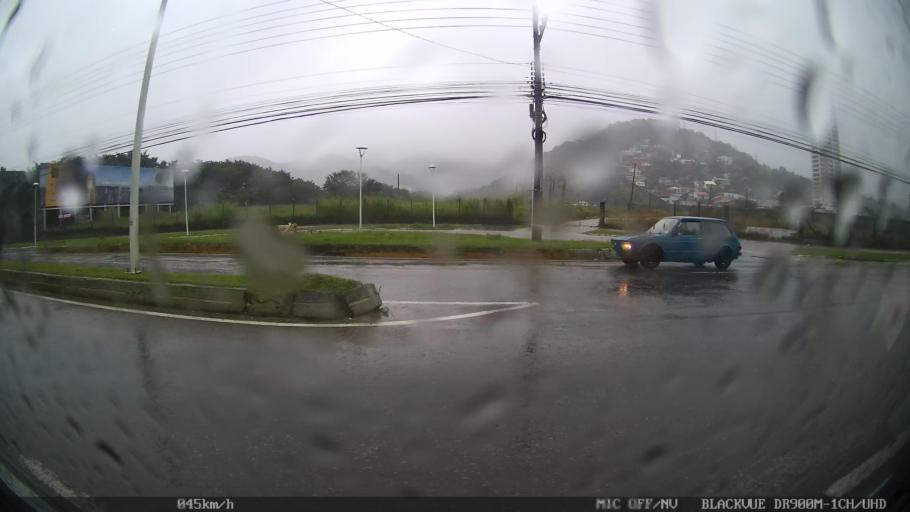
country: BR
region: Santa Catarina
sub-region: Balneario Camboriu
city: Balneario Camboriu
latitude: -26.9505
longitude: -48.6405
